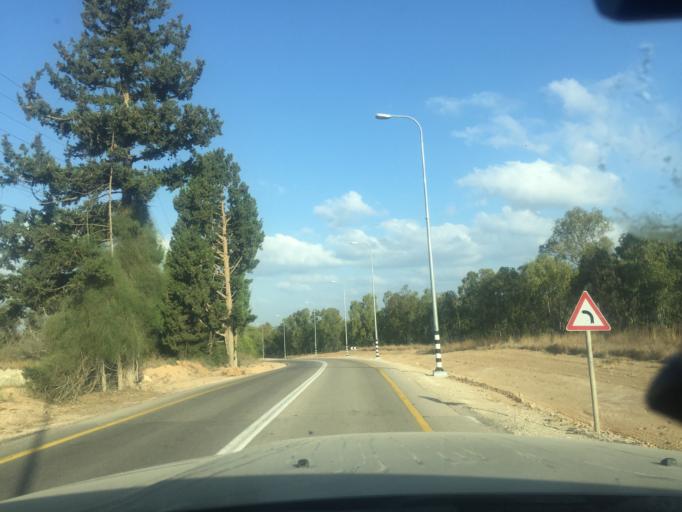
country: PS
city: Umm an Nasr
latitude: 31.6040
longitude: 34.5663
